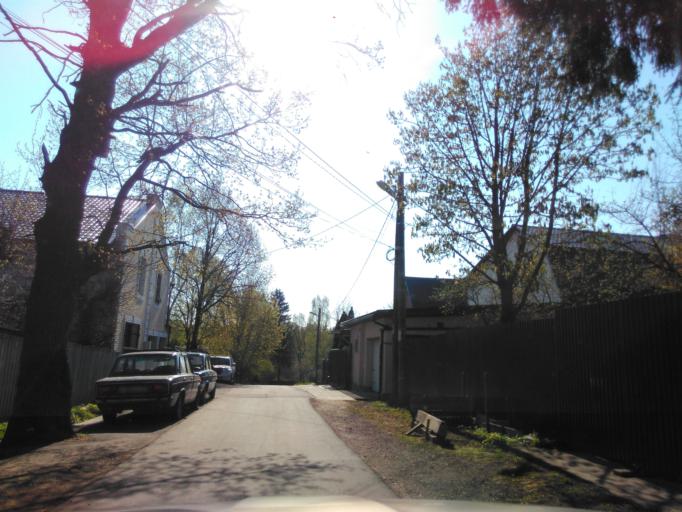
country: RU
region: Moskovskaya
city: Skhodnya
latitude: 55.9592
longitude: 37.2779
